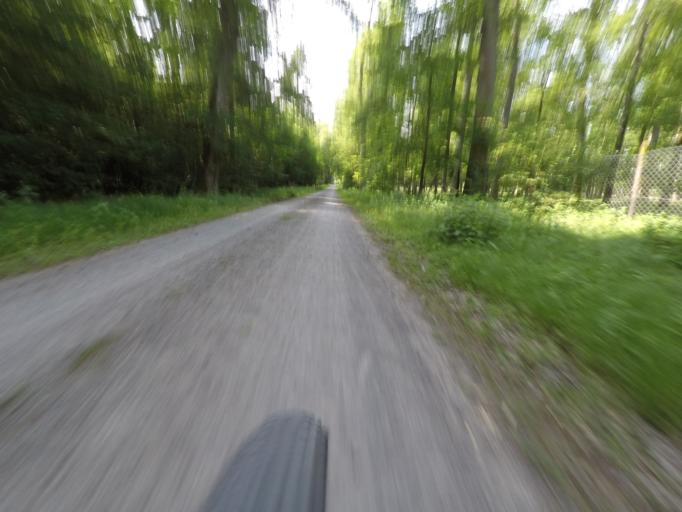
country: DE
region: Baden-Wuerttemberg
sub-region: Regierungsbezirk Stuttgart
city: Weil im Schonbuch
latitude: 48.5908
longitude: 9.0568
